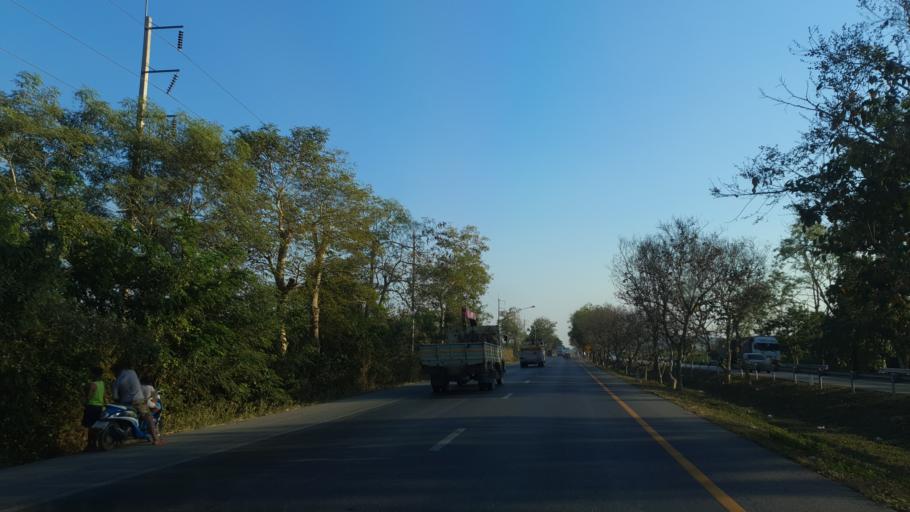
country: TH
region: Kamphaeng Phet
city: Khlong Khlung
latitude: 16.2253
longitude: 99.6989
